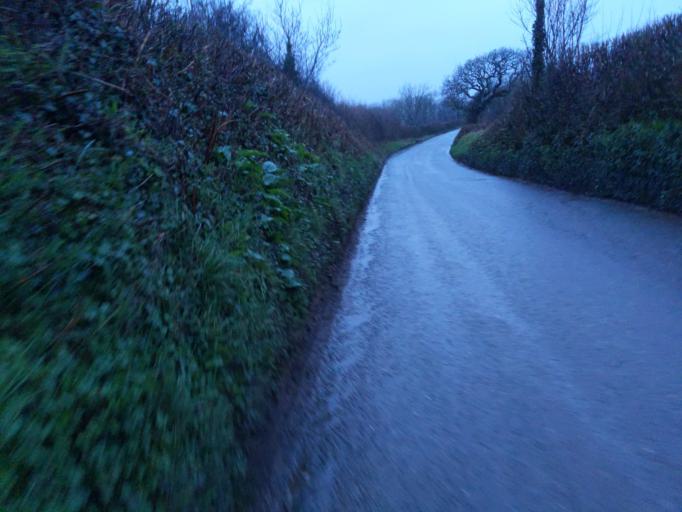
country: GB
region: England
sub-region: Devon
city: Yealmpton
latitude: 50.3349
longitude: -4.0143
